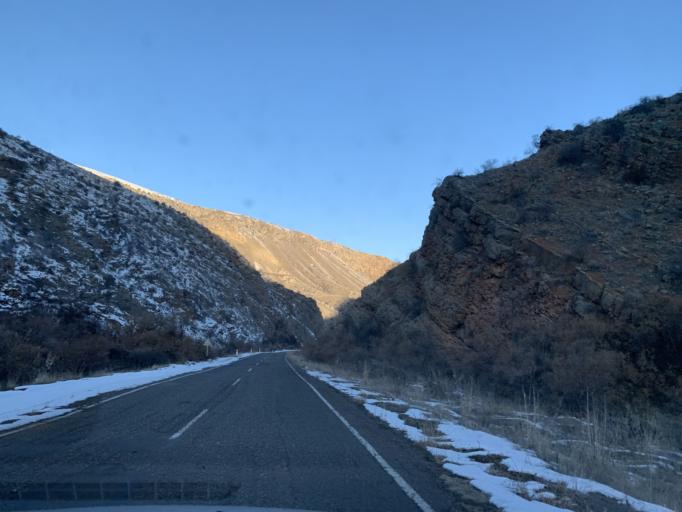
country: AM
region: Vayots' Dzori Marz
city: Areni
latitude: 39.6916
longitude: 45.2172
